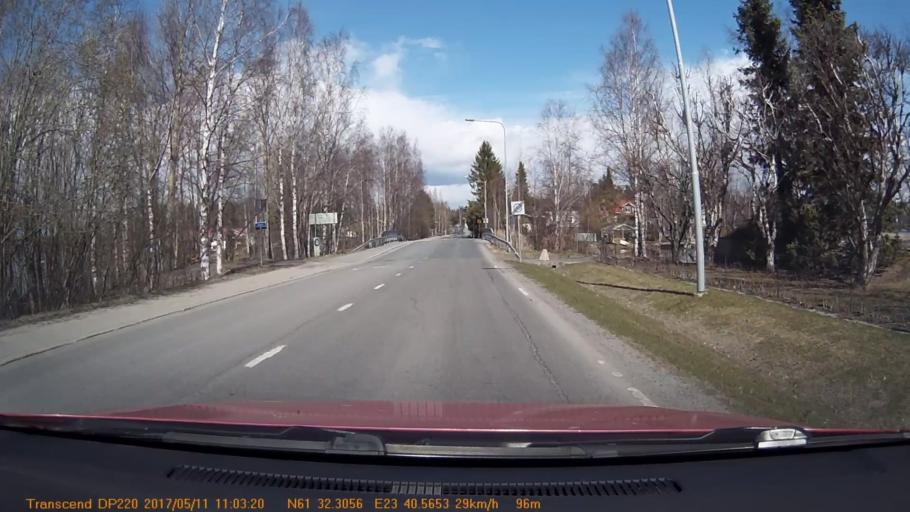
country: FI
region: Pirkanmaa
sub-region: Tampere
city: Yloejaervi
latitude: 61.5383
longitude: 23.6760
